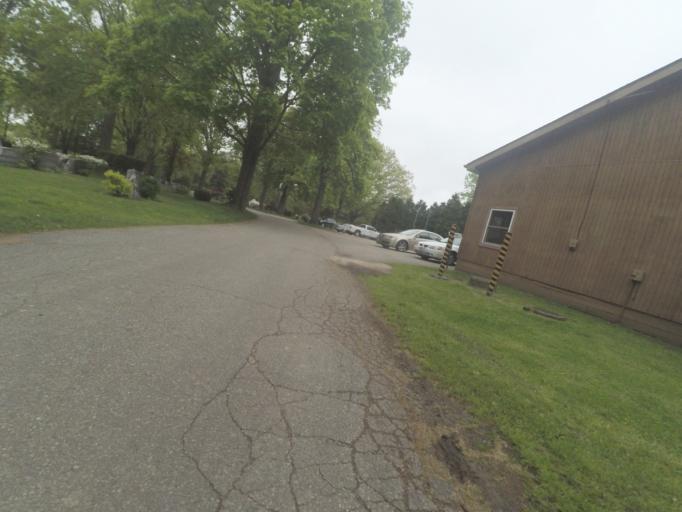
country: US
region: Ohio
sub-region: Portage County
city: Kent
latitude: 41.1663
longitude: -81.3519
